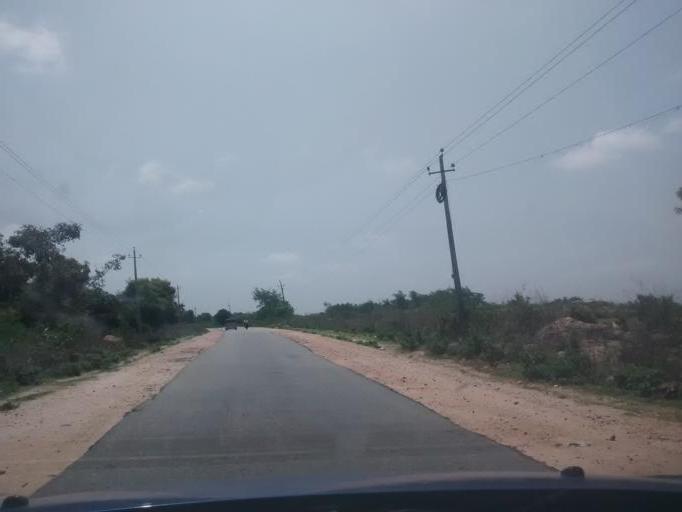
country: IN
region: Karnataka
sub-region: Mandya
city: Krishnarajpet
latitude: 12.5775
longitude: 76.3228
